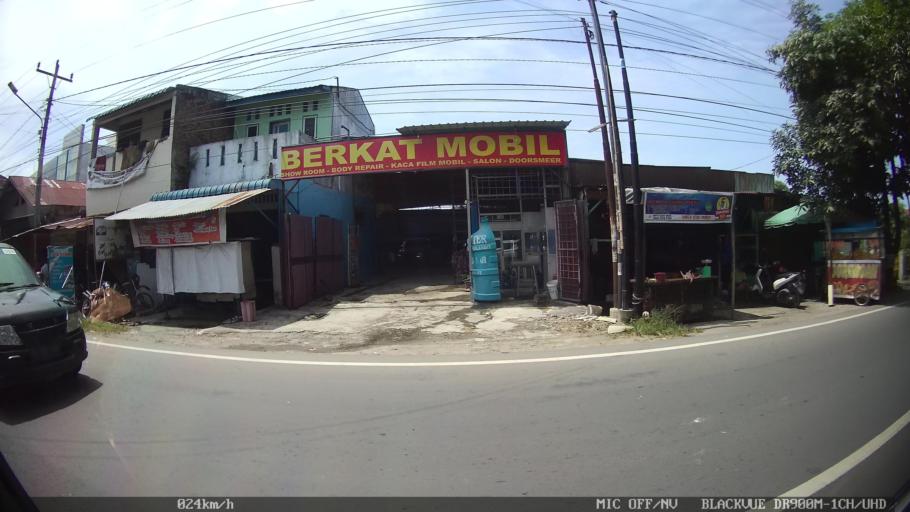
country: ID
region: North Sumatra
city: Sunggal
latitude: 3.5793
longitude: 98.6309
